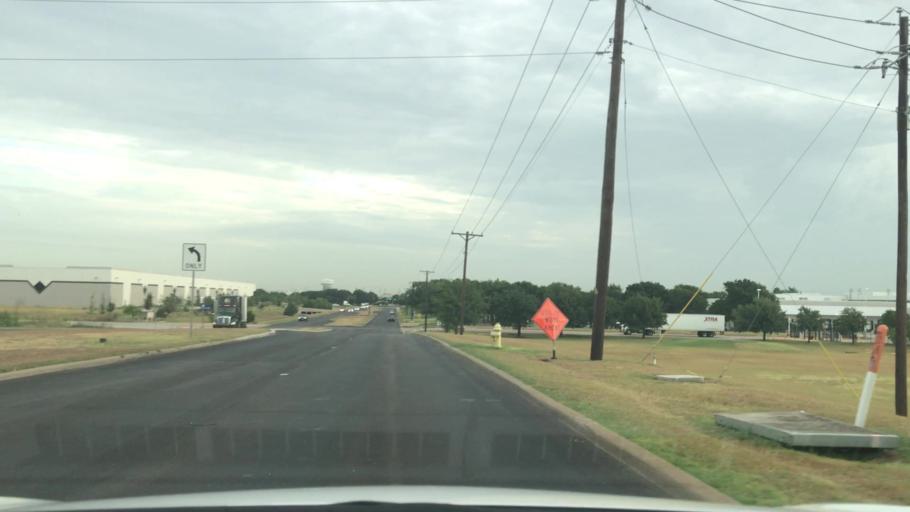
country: US
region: Texas
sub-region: Dallas County
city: Coppell
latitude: 32.9491
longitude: -97.0221
